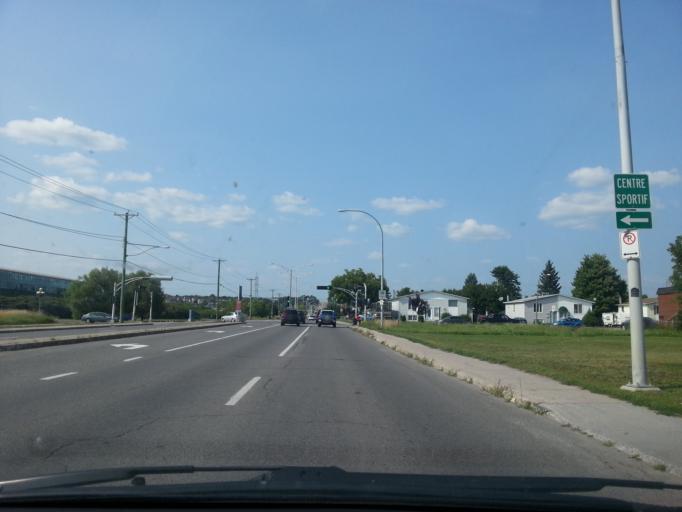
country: CA
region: Quebec
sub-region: Outaouais
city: Gatineau
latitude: 45.4856
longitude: -75.6747
